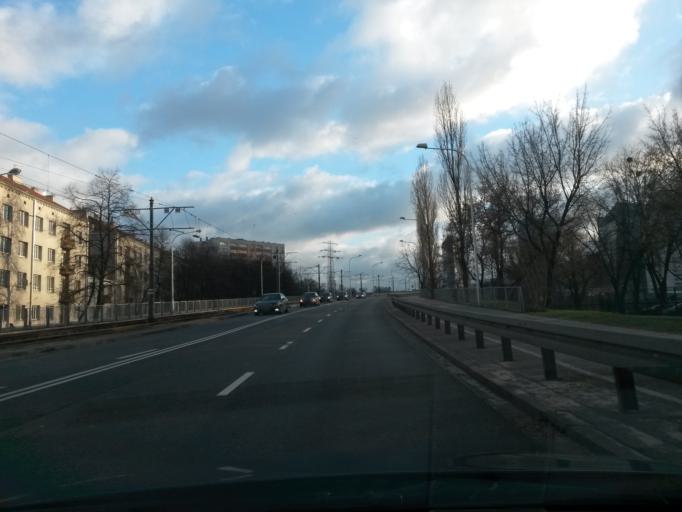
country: PL
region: Masovian Voivodeship
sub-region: Warszawa
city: Zoliborz
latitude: 52.2614
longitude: 20.9934
